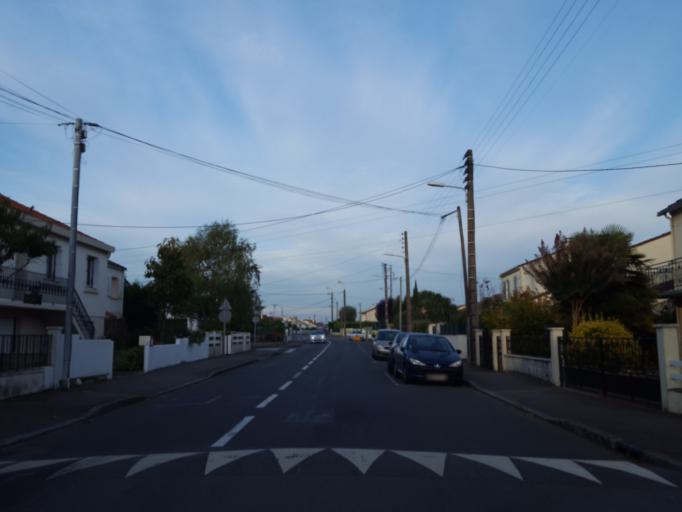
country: FR
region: Pays de la Loire
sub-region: Departement de la Loire-Atlantique
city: Saint-Sebastien-sur-Loire
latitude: 47.1996
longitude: -1.4959
